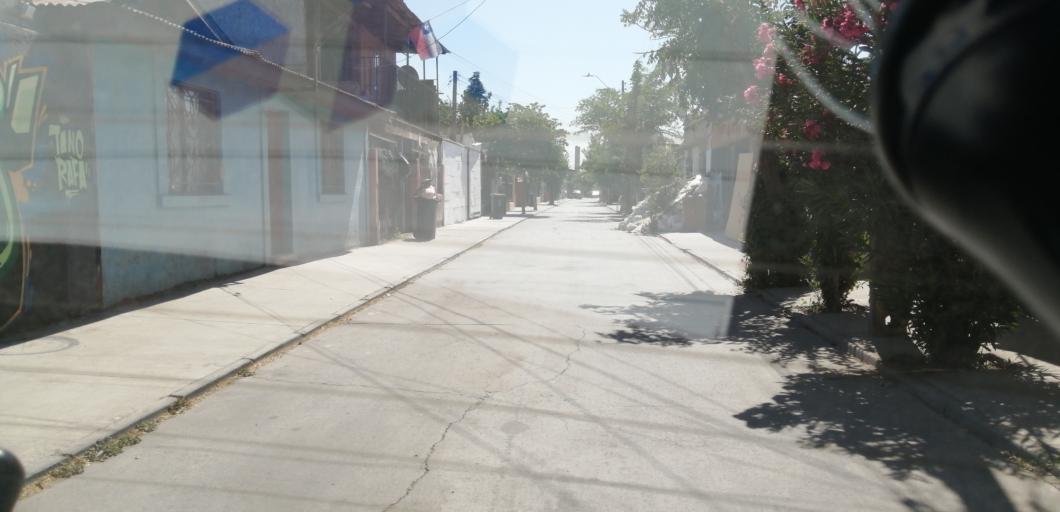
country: CL
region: Santiago Metropolitan
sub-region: Provincia de Santiago
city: Lo Prado
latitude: -33.4345
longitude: -70.7539
